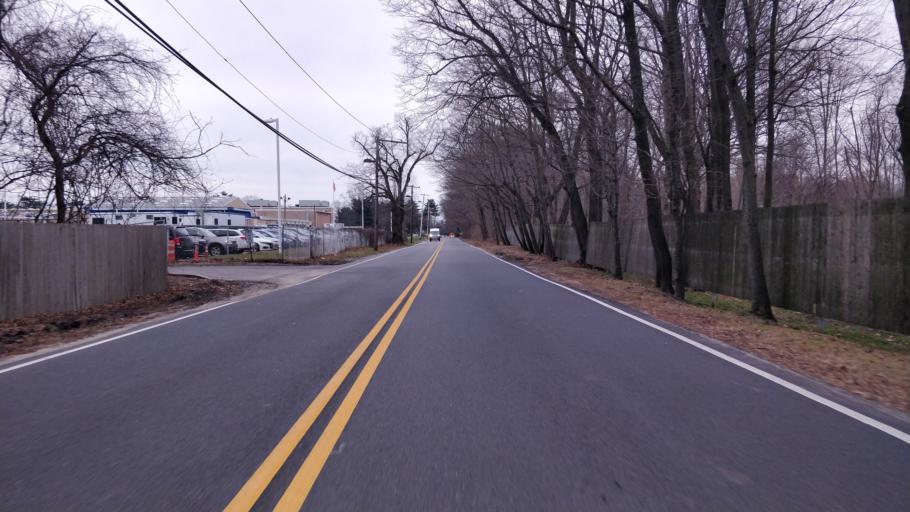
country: US
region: New York
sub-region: Nassau County
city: Westbury
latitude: 40.7710
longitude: -73.5891
